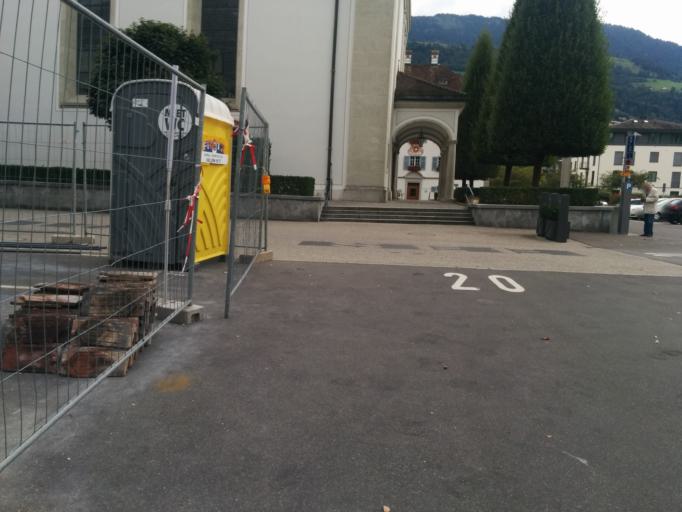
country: CH
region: Schwyz
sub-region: Bezirk Kuessnacht
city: Kussnacht
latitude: 47.0805
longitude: 8.4395
